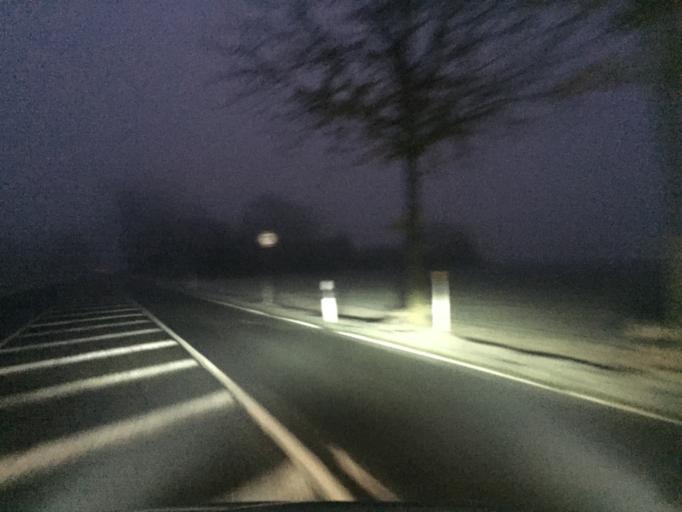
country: DE
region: Lower Saxony
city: Kirchdorf
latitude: 52.6096
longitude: 8.8952
